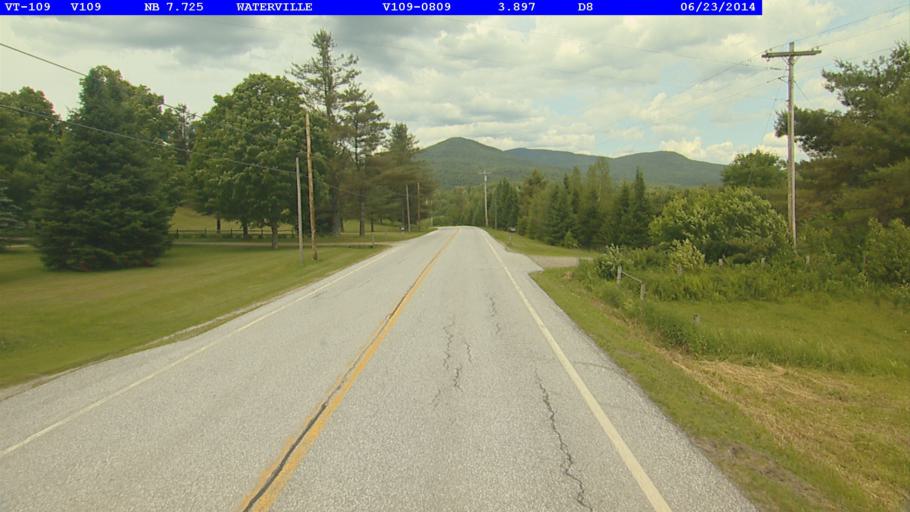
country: US
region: Vermont
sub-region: Lamoille County
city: Johnson
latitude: 44.7330
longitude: -72.7459
